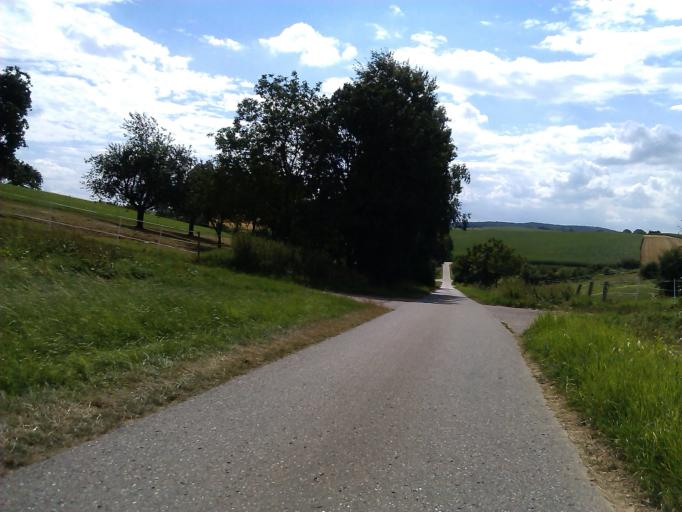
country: DE
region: Baden-Wuerttemberg
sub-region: Regierungsbezirk Stuttgart
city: Ittlingen
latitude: 49.1831
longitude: 8.8665
